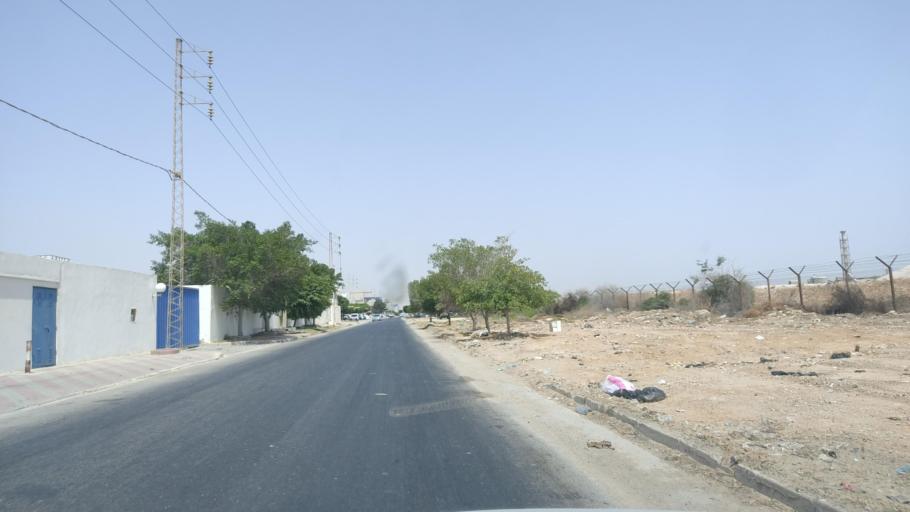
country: TN
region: Safaqis
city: Sfax
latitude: 34.6935
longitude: 10.7257
